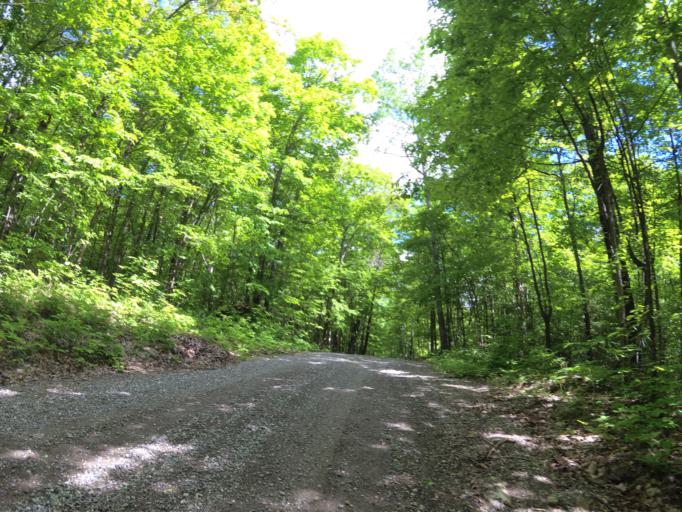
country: CA
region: Ontario
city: Renfrew
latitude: 45.0677
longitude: -76.7614
